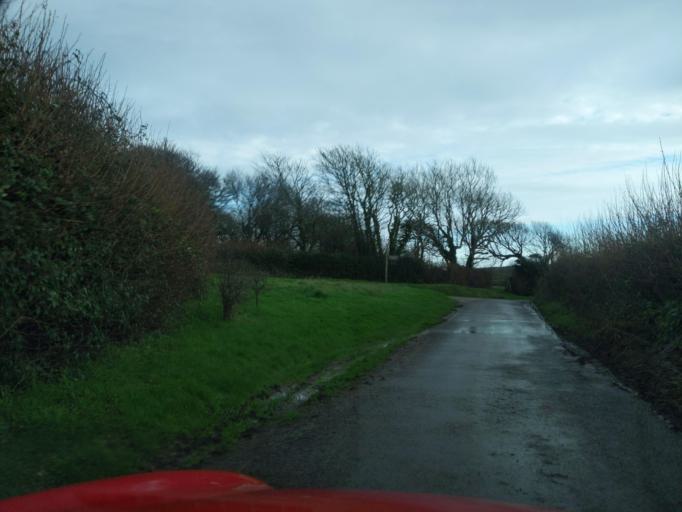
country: GB
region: England
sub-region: Devon
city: Salcombe
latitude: 50.2609
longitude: -3.6828
